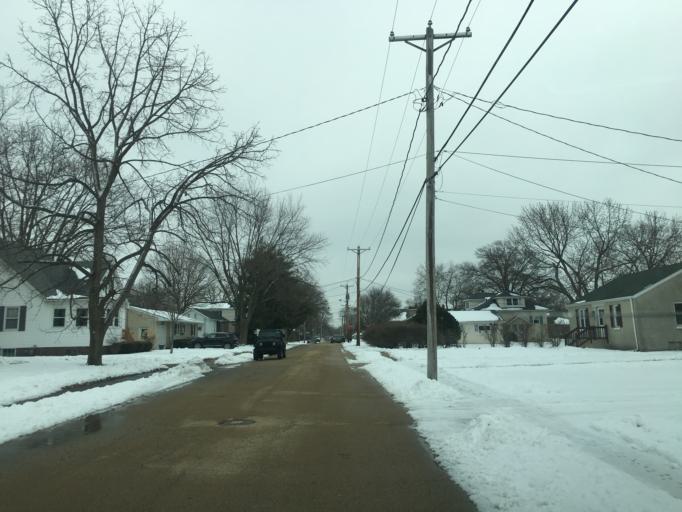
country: US
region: Illinois
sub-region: LaSalle County
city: Peru
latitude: 41.3312
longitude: -89.1355
